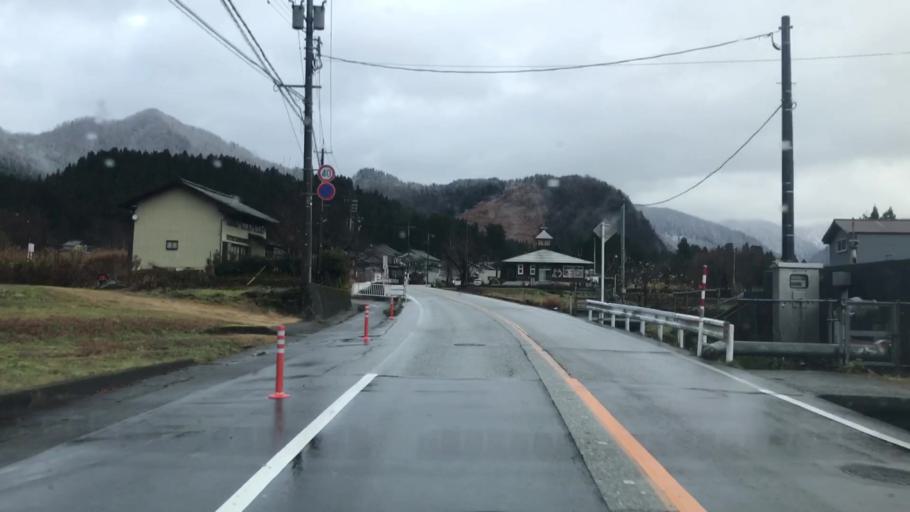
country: JP
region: Toyama
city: Kamiichi
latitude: 36.5796
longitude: 137.3873
